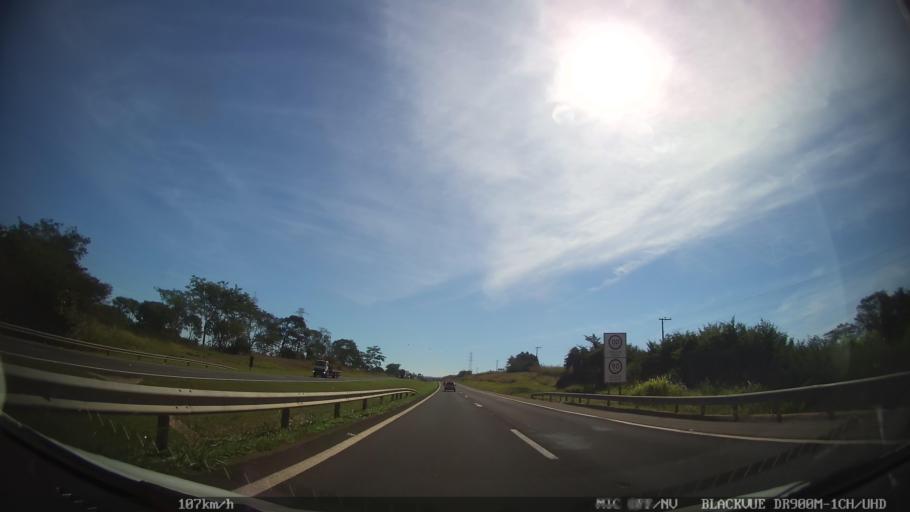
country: BR
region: Sao Paulo
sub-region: Porto Ferreira
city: Porto Ferreira
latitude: -21.8216
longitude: -47.4958
